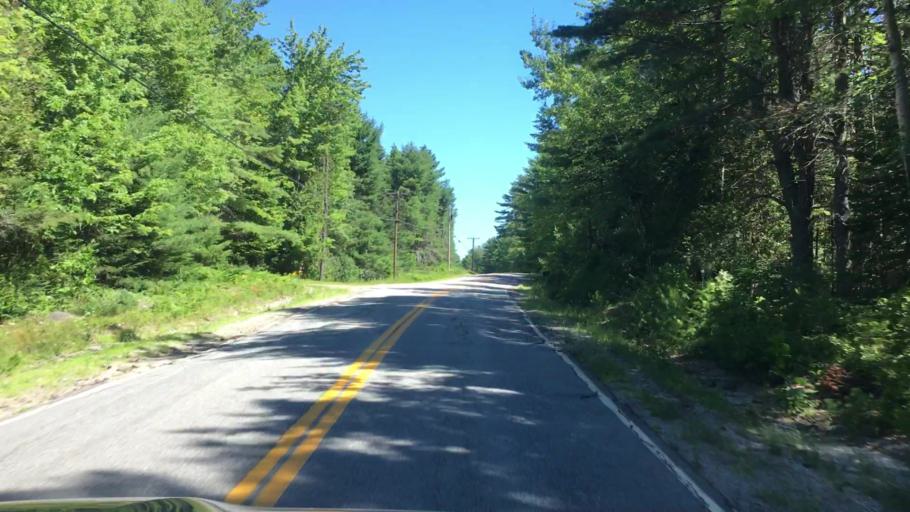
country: US
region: Maine
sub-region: Hancock County
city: Penobscot
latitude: 44.5085
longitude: -68.6754
